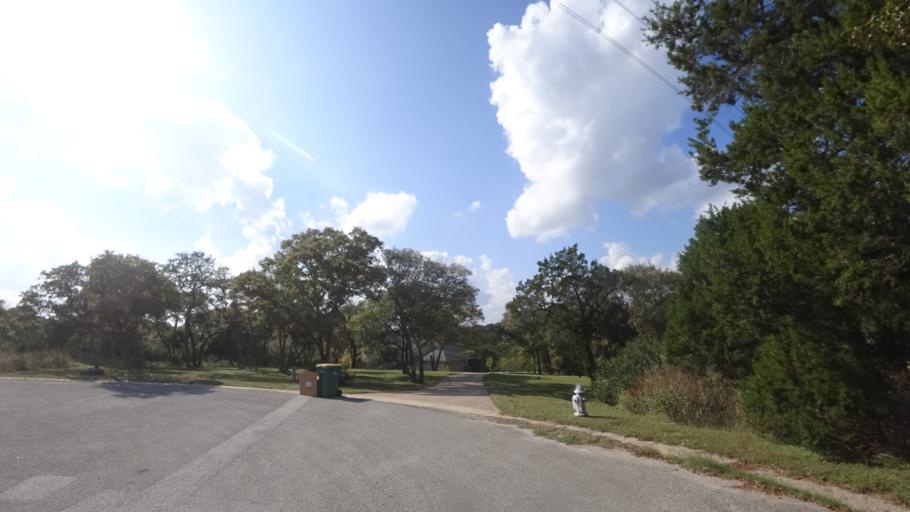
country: US
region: Texas
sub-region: Travis County
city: Lost Creek
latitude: 30.3109
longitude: -97.8546
